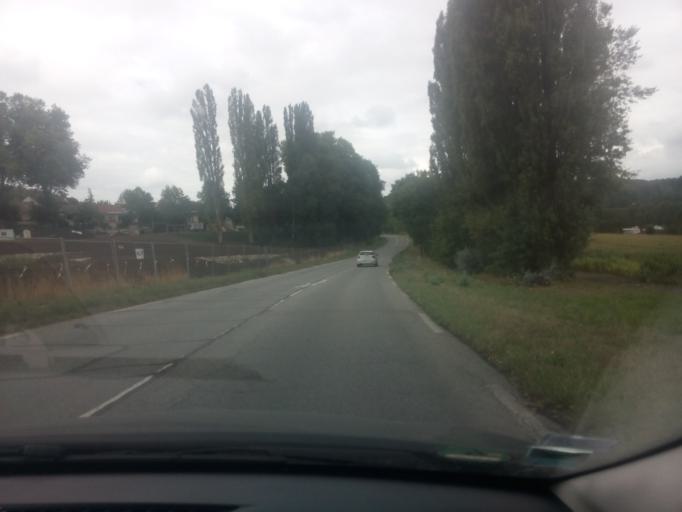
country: FR
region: Ile-de-France
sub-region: Departement des Yvelines
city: Jouy-en-Josas
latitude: 48.7586
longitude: 2.1870
